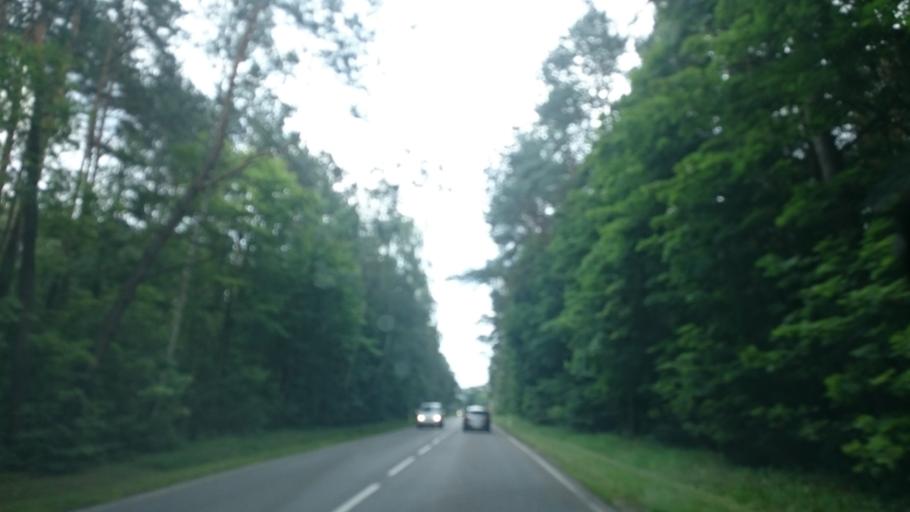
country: PL
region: Kujawsko-Pomorskie
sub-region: Powiat tucholski
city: Cekcyn
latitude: 53.5223
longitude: 17.9504
